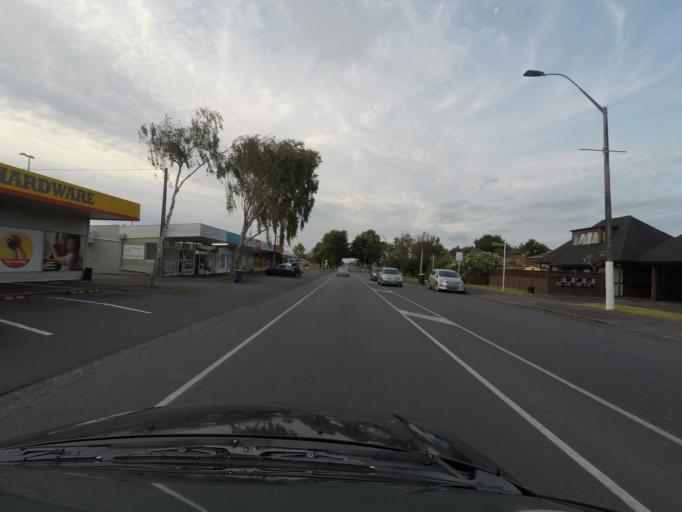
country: NZ
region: Auckland
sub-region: Auckland
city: Rosebank
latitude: -36.8405
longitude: 174.6516
